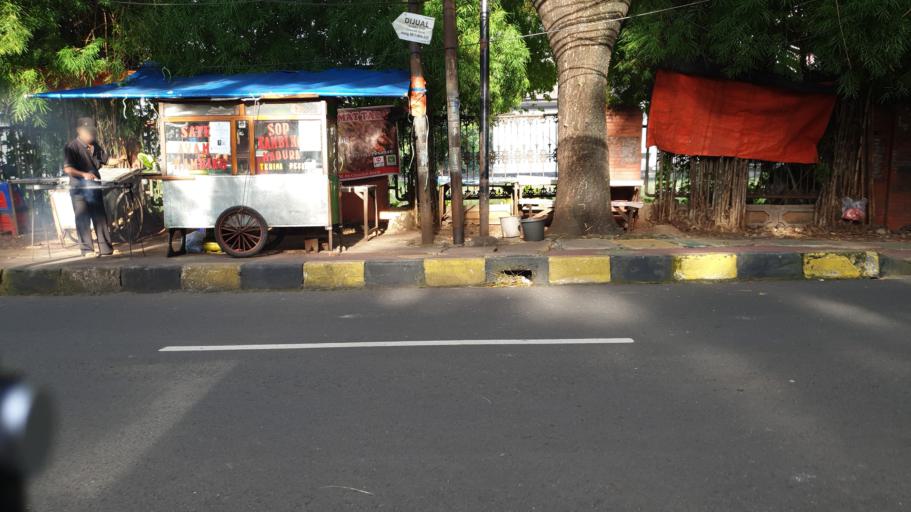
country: ID
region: Banten
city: South Tangerang
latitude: -6.2907
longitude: 106.7909
